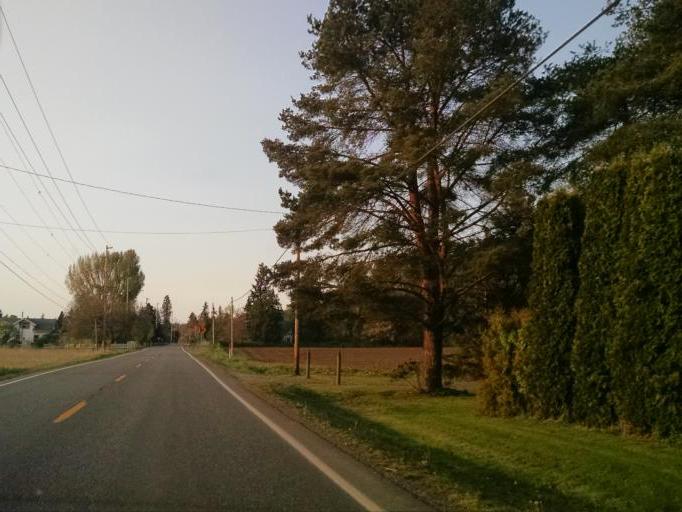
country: US
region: Washington
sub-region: Whatcom County
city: Nooksack
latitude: 48.8478
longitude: -122.2886
